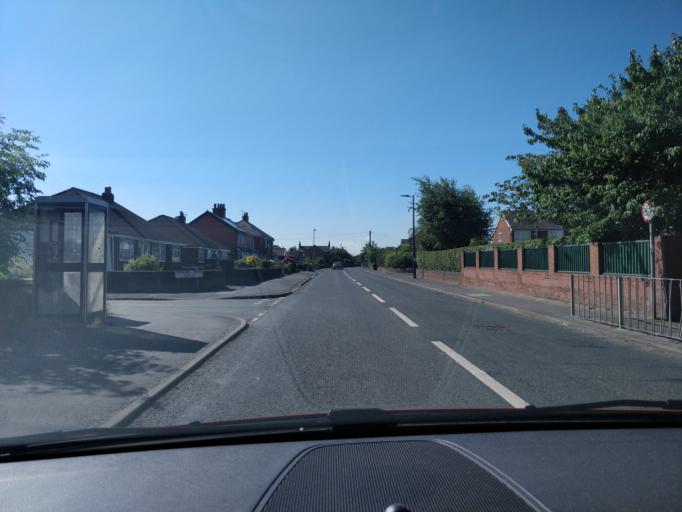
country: GB
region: England
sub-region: Lancashire
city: Tarleton
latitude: 53.6893
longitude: -2.8340
